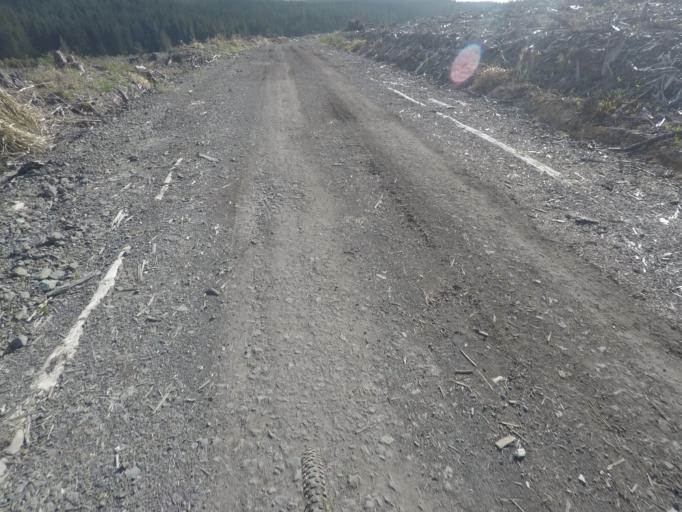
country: NZ
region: Auckland
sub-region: Auckland
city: Parakai
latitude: -36.7138
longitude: 174.5676
